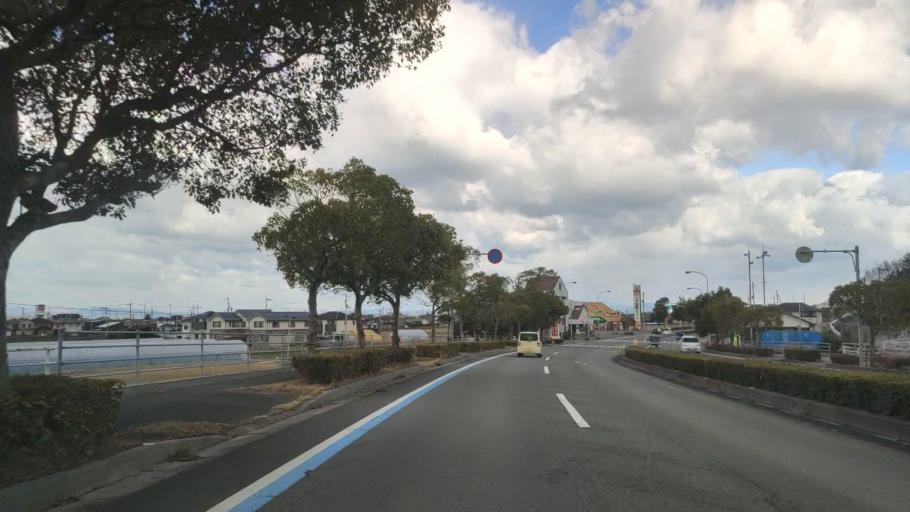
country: JP
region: Ehime
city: Hojo
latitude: 33.9480
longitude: 132.7746
